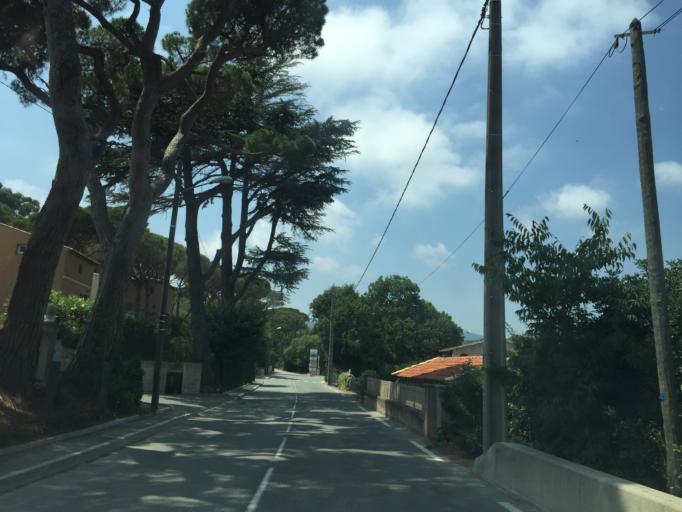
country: FR
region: Provence-Alpes-Cote d'Azur
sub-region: Departement du Var
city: Sainte-Maxime
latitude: 43.3433
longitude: 6.6785
